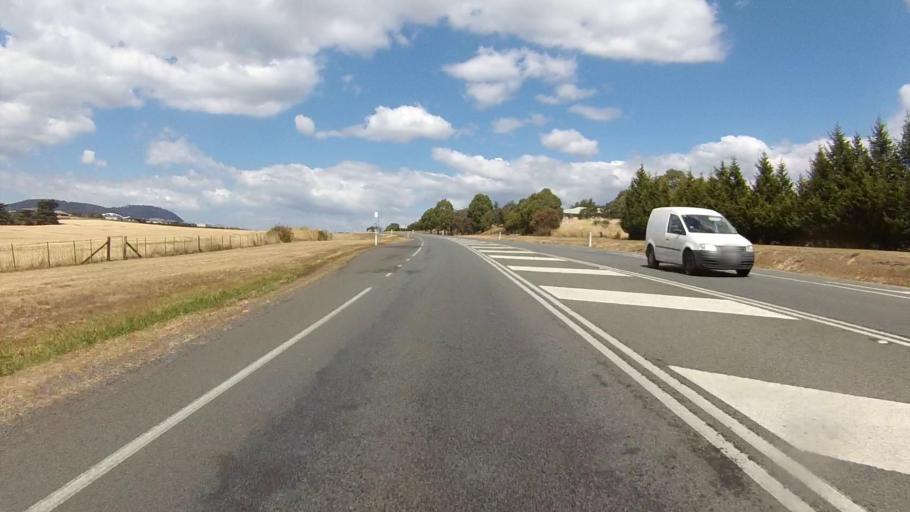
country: AU
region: Tasmania
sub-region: Brighton
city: Old Beach
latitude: -42.7583
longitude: 147.2678
